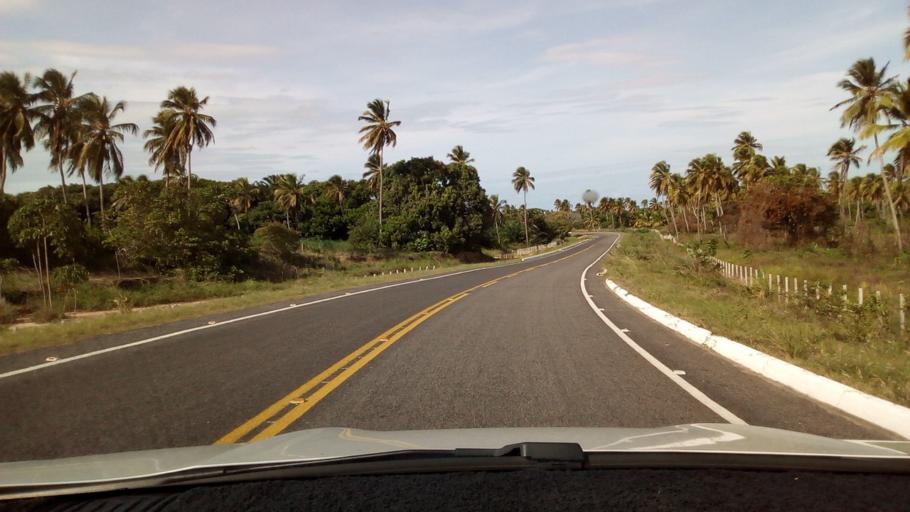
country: BR
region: Paraiba
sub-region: Cabedelo
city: Cabedelo
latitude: -6.9996
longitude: -34.8839
